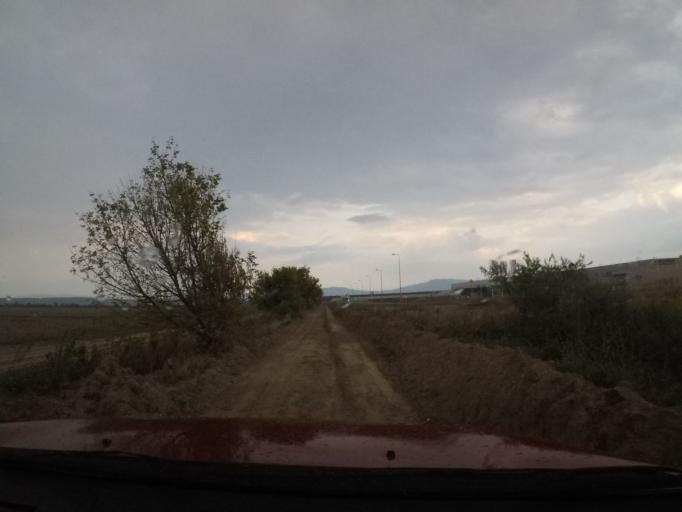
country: SK
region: Kosicky
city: Kosice
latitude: 48.6801
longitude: 21.2263
